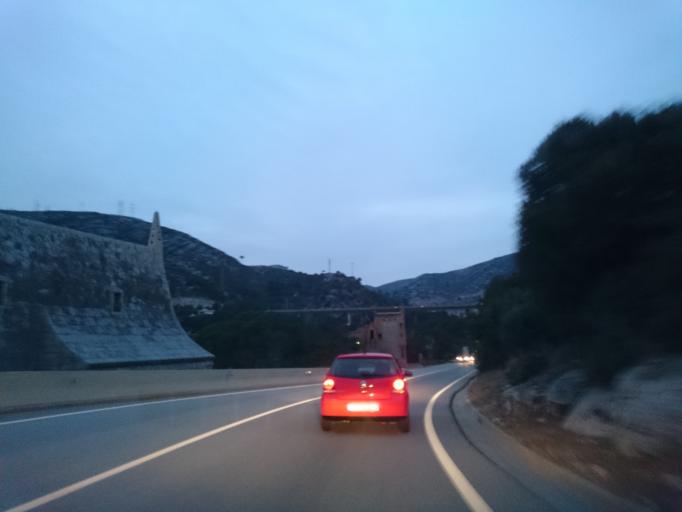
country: ES
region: Catalonia
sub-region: Provincia de Barcelona
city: Castelldefels
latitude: 41.2559
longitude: 1.9060
